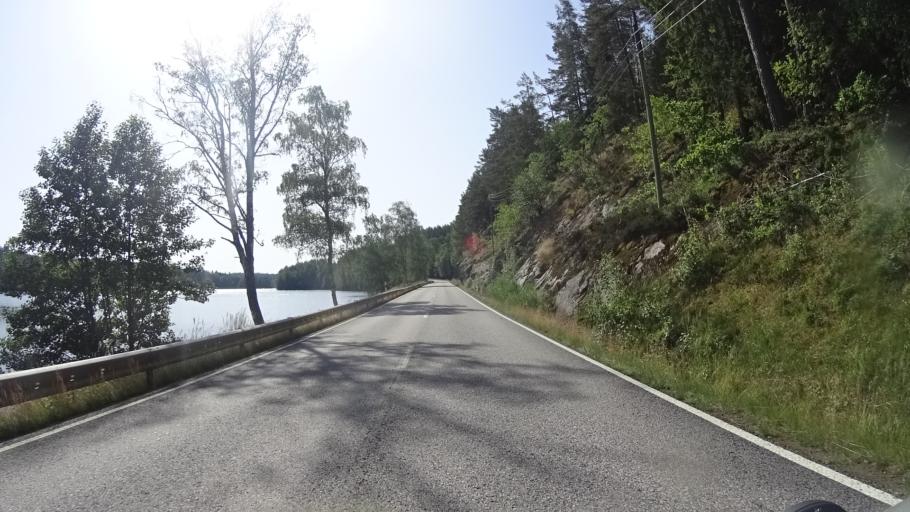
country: SE
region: Kalmar
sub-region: Vasterviks Kommun
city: Overum
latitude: 58.0027
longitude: 16.2759
